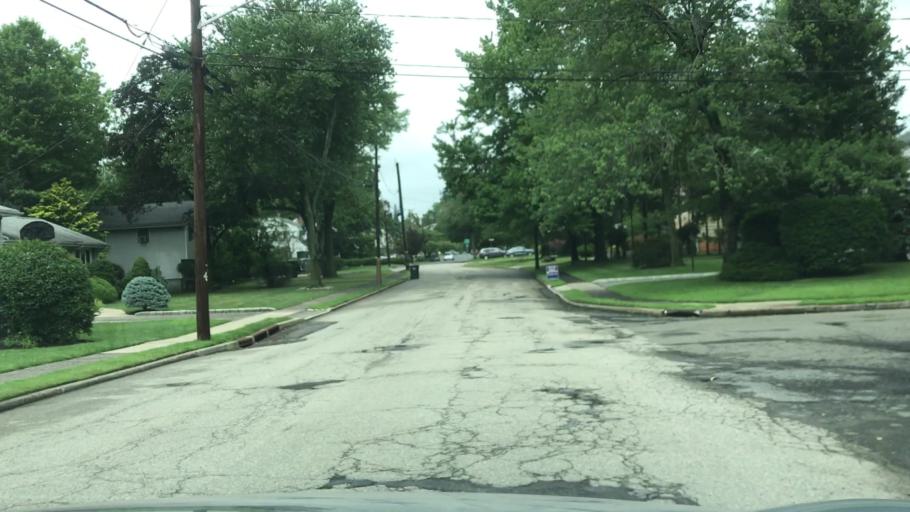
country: US
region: New Jersey
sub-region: Bergen County
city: Bergenfield
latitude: 40.9201
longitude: -73.9913
